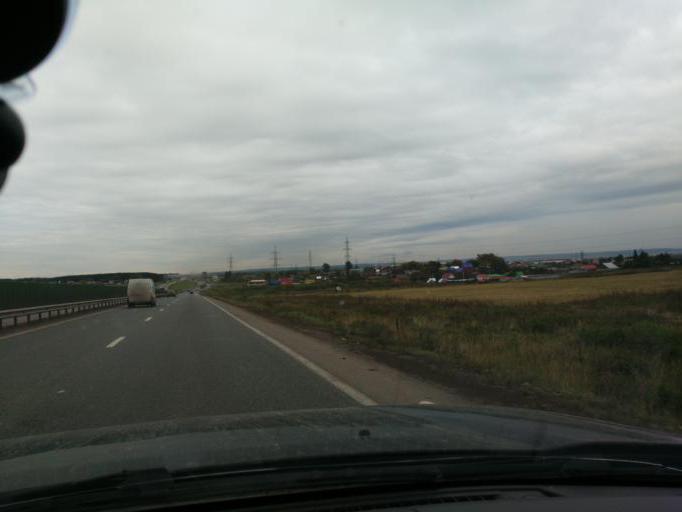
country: RU
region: Perm
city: Froly
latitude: 57.9347
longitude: 56.2281
